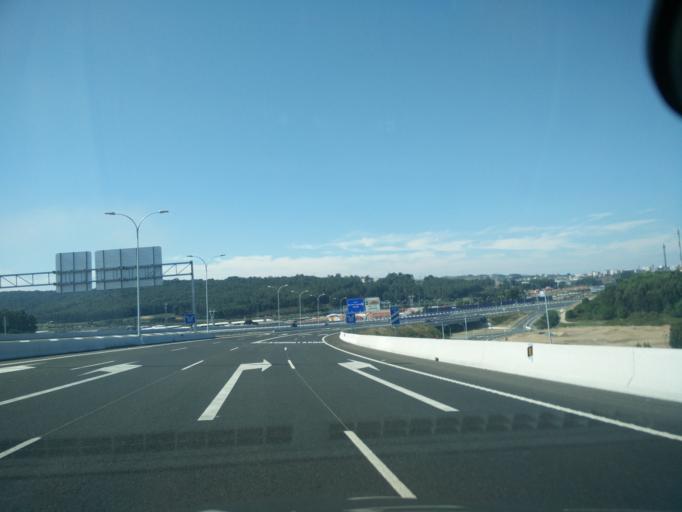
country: ES
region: Galicia
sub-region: Provincia da Coruna
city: Culleredo
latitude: 43.3263
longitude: -8.4217
